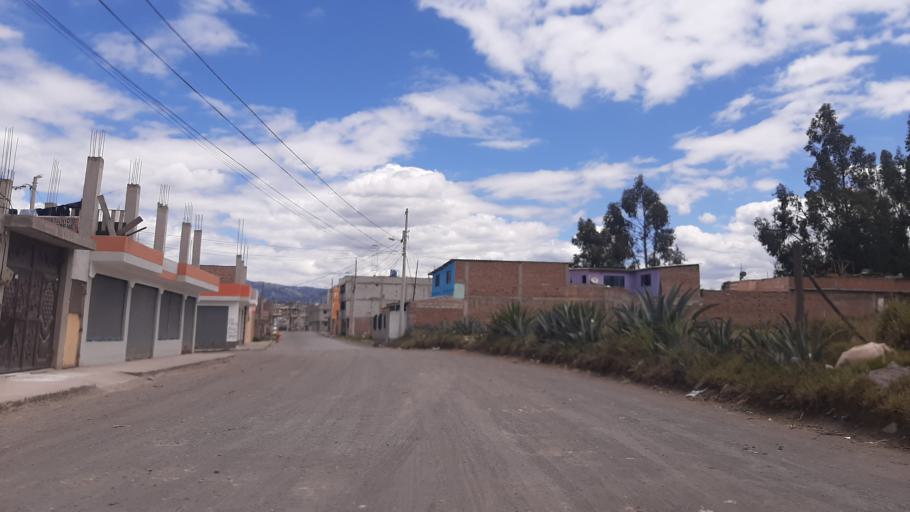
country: EC
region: Chimborazo
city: Riobamba
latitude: -1.6560
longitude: -78.6375
